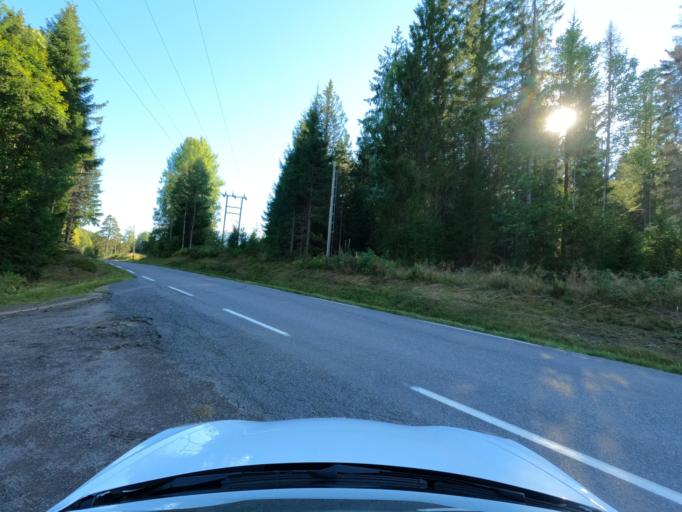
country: NO
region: Vestfold
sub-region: Andebu
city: Andebu
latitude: 59.3271
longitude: 10.0893
